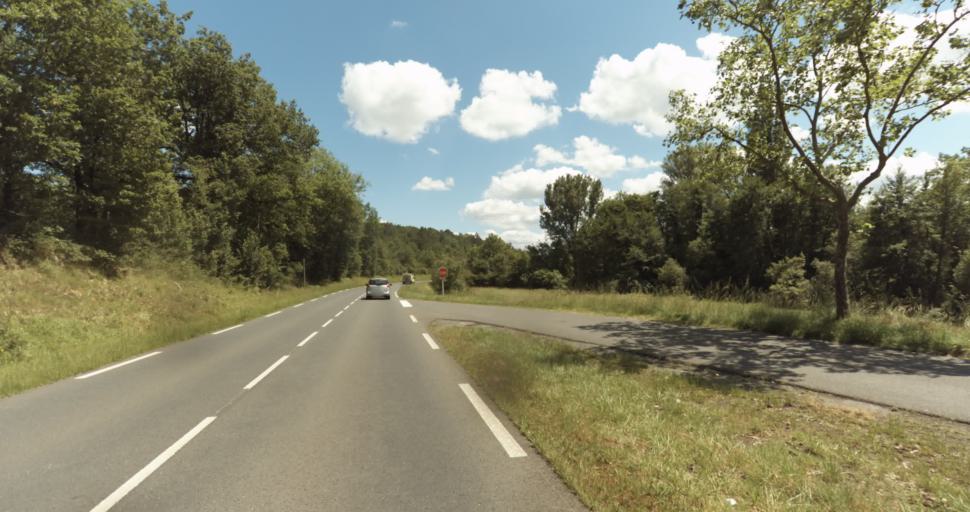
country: FR
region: Aquitaine
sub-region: Departement de la Dordogne
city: Le Bugue
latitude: 44.8452
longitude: 0.8480
